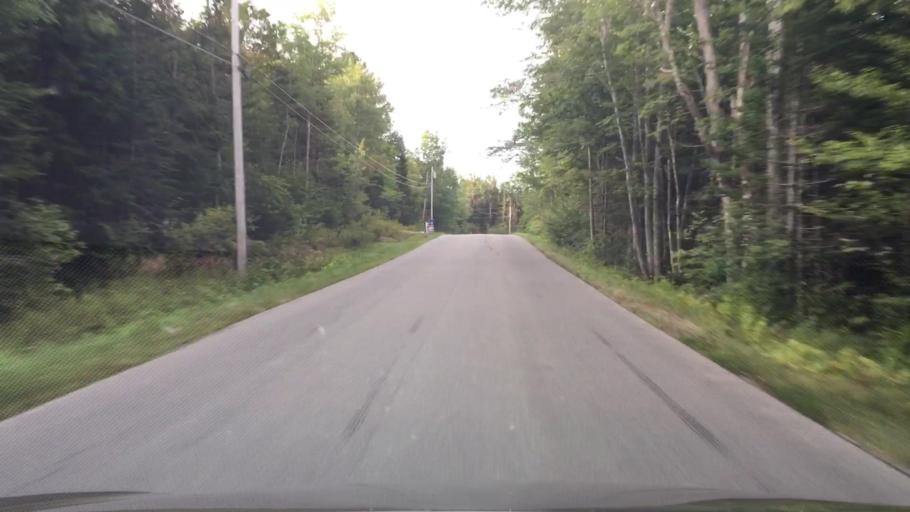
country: US
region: Maine
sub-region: Waldo County
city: Stockton Springs
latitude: 44.4960
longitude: -68.8742
